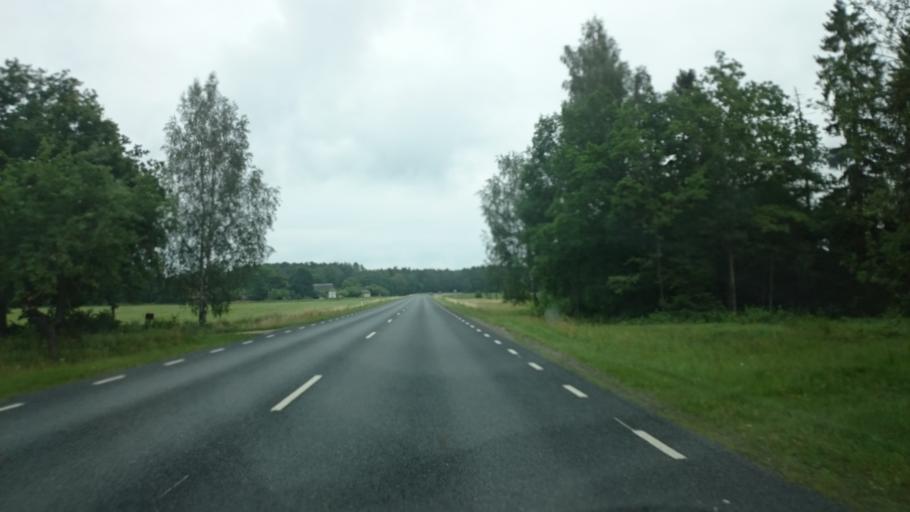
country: EE
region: Saare
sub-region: Orissaare vald
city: Orissaare
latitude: 58.6023
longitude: 23.3107
